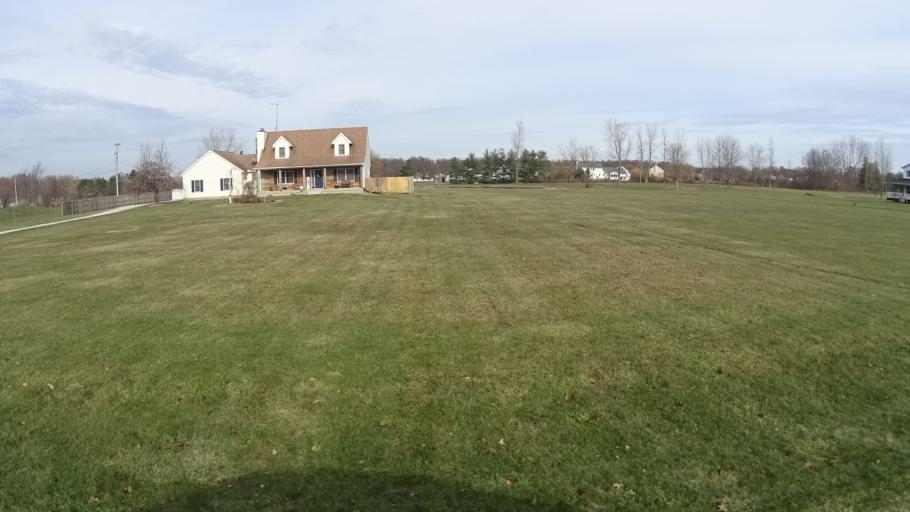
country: US
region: Ohio
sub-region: Lorain County
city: Grafton
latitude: 41.2229
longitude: -82.0389
